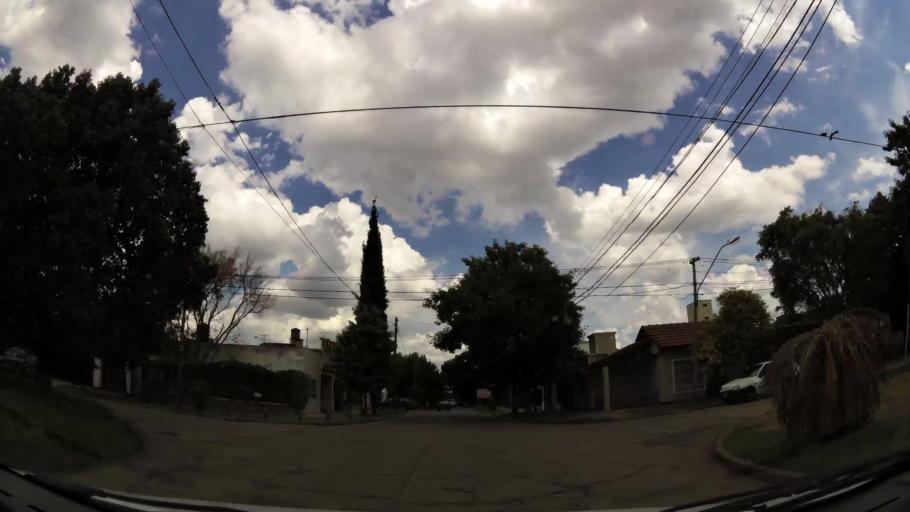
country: AR
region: Buenos Aires
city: Ituzaingo
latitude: -34.6533
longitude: -58.6670
